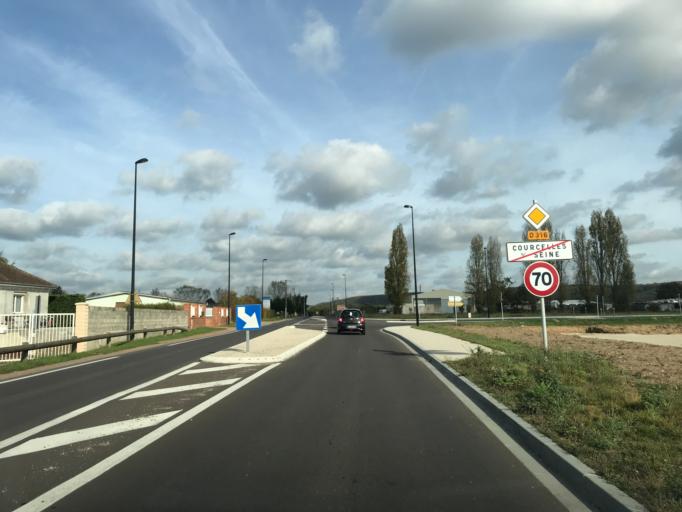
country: FR
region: Haute-Normandie
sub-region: Departement de l'Eure
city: Courcelles-sur-Seine
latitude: 49.1873
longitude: 1.3649
